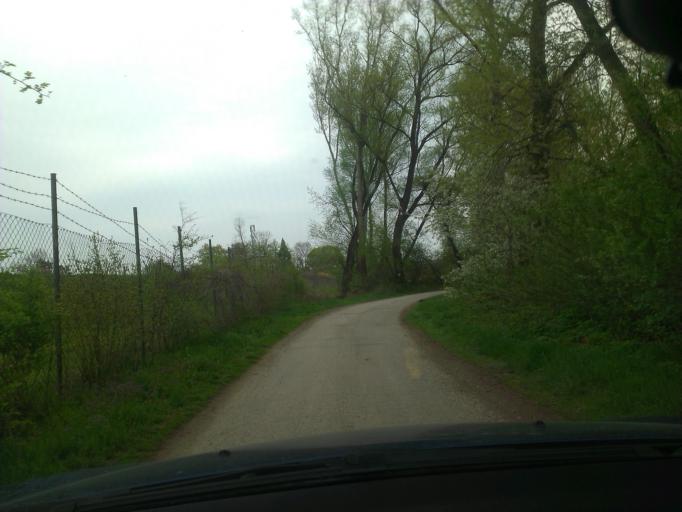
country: SK
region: Trnavsky
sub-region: Okres Trnava
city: Piestany
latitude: 48.5448
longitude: 17.8134
